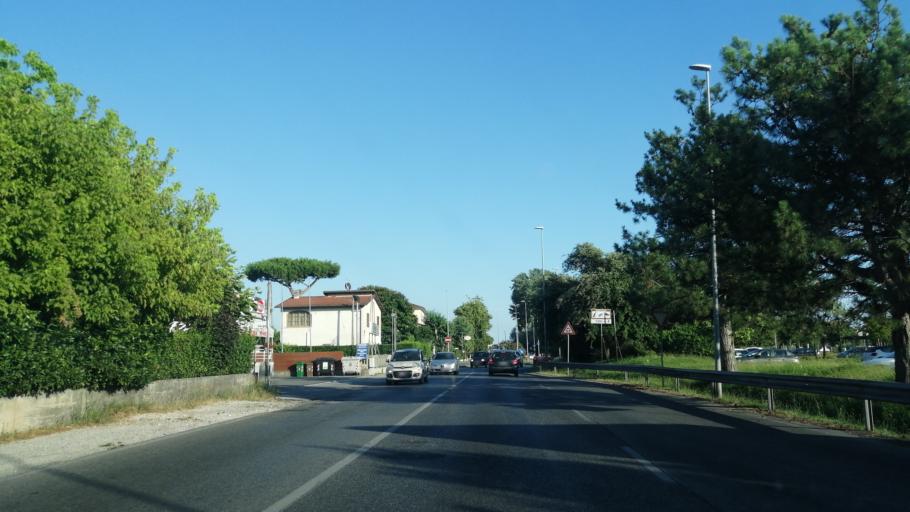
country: IT
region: Tuscany
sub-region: Provincia di Lucca
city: Camaiore
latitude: 43.9118
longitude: 10.2236
